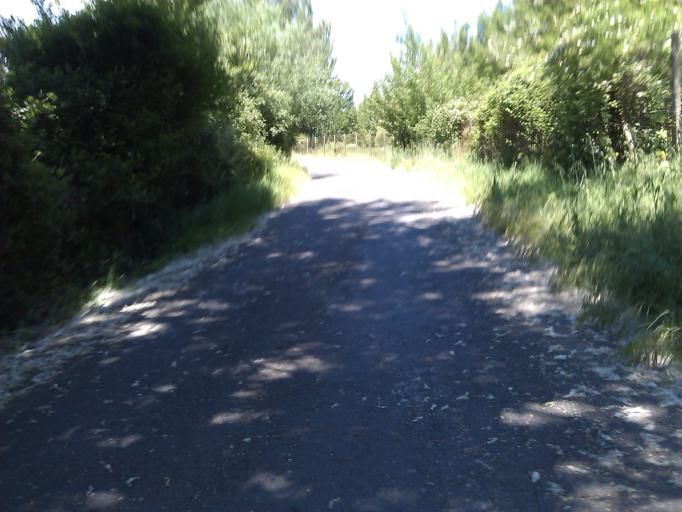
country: ES
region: Castille and Leon
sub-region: Provincia de Leon
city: Leon
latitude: 42.5922
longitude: -5.5494
